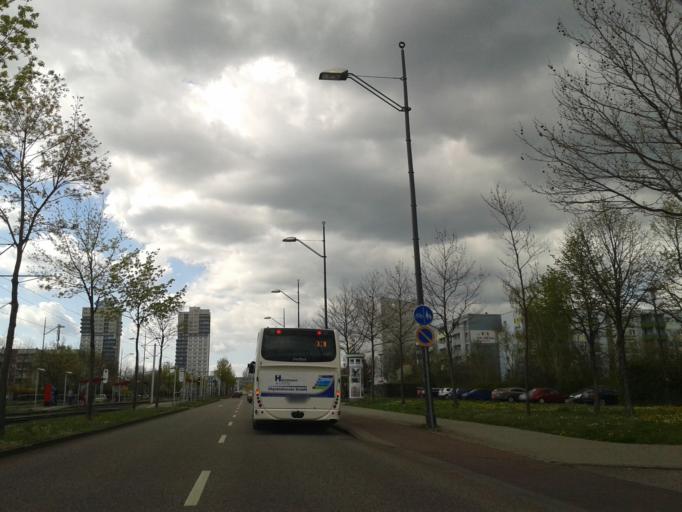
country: DE
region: Saxony-Anhalt
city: Halle Neustadt
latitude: 51.4791
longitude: 11.9093
